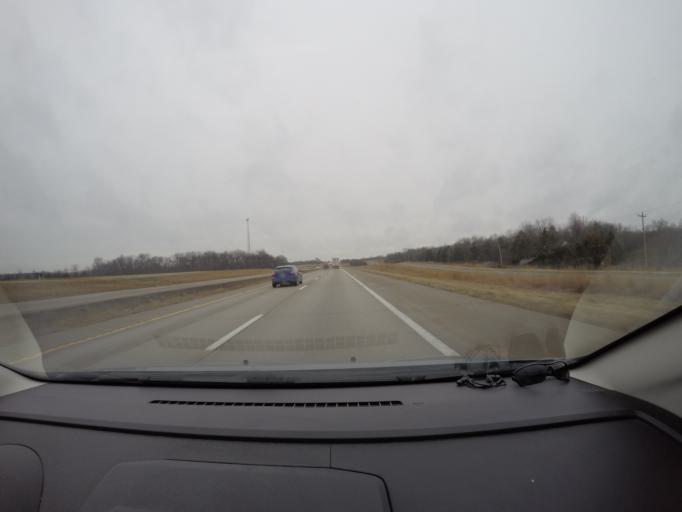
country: US
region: Missouri
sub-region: Montgomery County
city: Montgomery City
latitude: 38.9064
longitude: -91.6497
